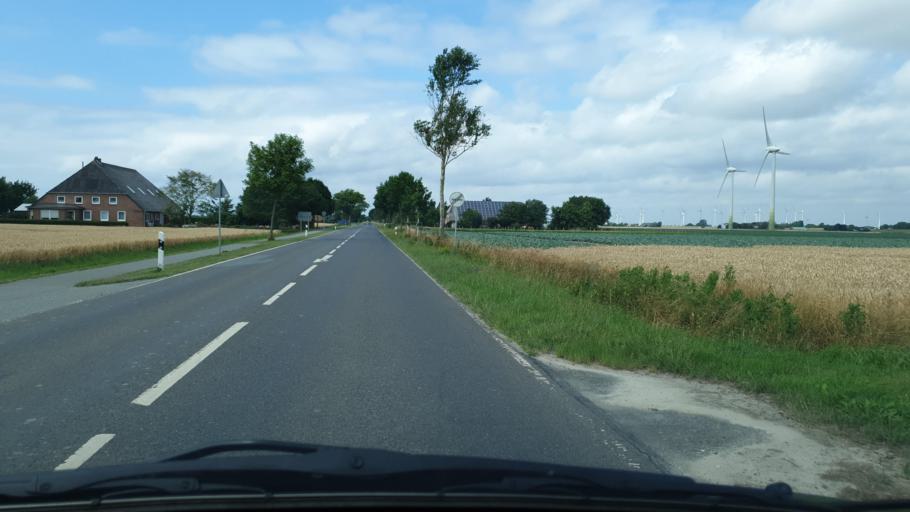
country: DE
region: Schleswig-Holstein
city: Friedrichskoog
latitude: 53.9752
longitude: 8.9220
